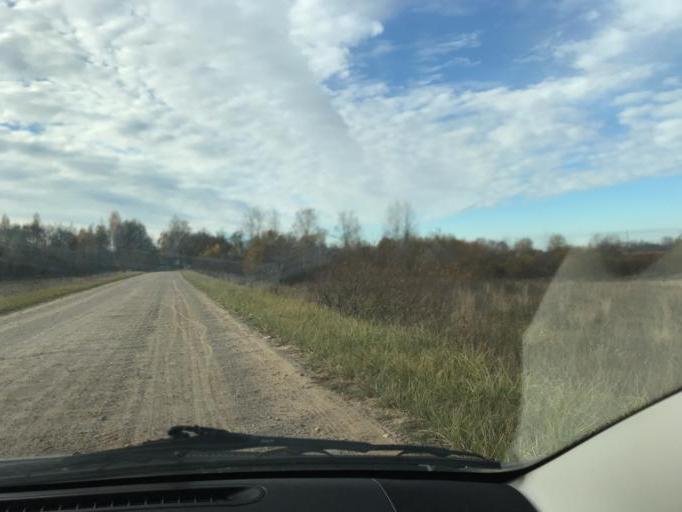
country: BY
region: Vitebsk
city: Haradok
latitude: 55.4560
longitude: 30.0418
